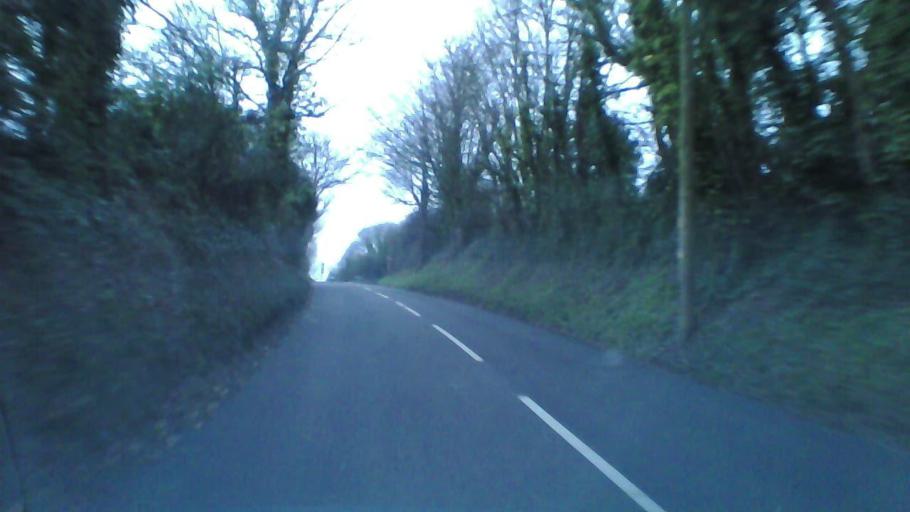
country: GB
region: England
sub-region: Isle of Wight
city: Brading
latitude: 50.6759
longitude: -1.1461
